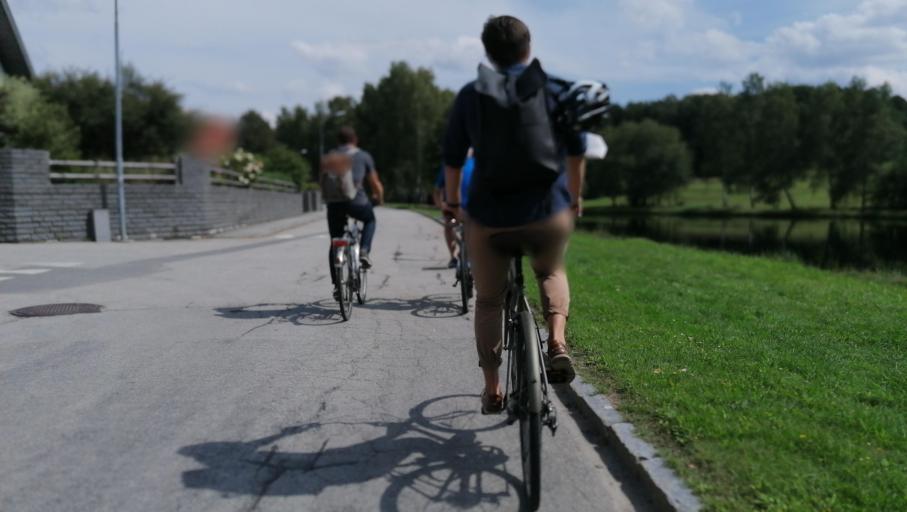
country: AT
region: Lower Austria
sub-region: Politischer Bezirk Gmund
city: Schrems
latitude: 48.7945
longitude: 15.0816
